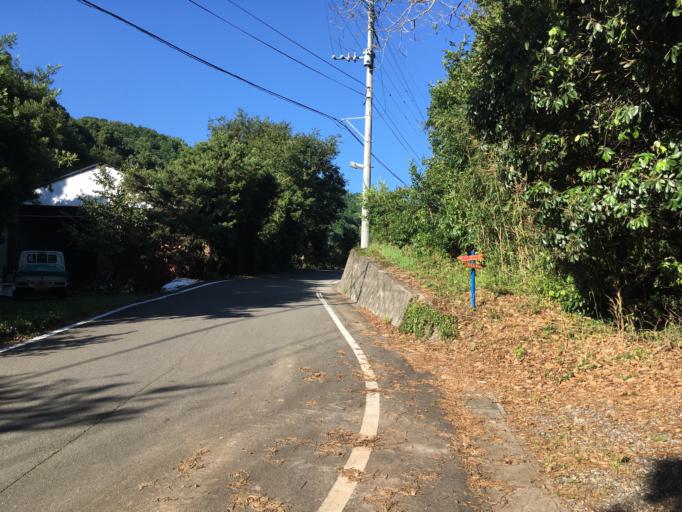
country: JP
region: Kumamoto
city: Kumamoto
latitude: 32.7980
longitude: 130.6624
